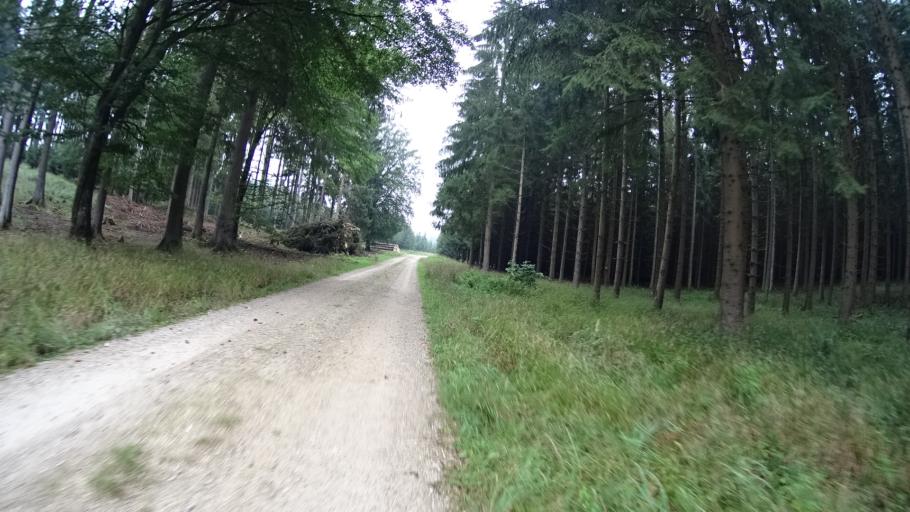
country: DE
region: Bavaria
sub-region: Upper Bavaria
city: Stammham
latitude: 48.8979
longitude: 11.5045
